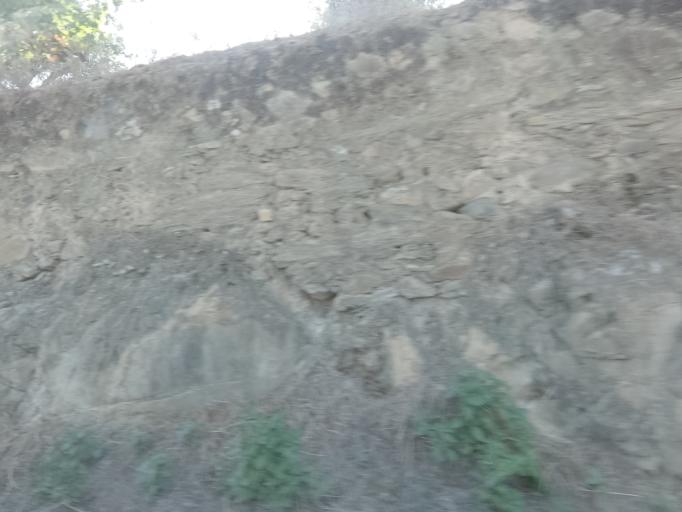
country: PT
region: Vila Real
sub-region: Sabrosa
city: Vilela
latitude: 41.1822
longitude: -7.5528
